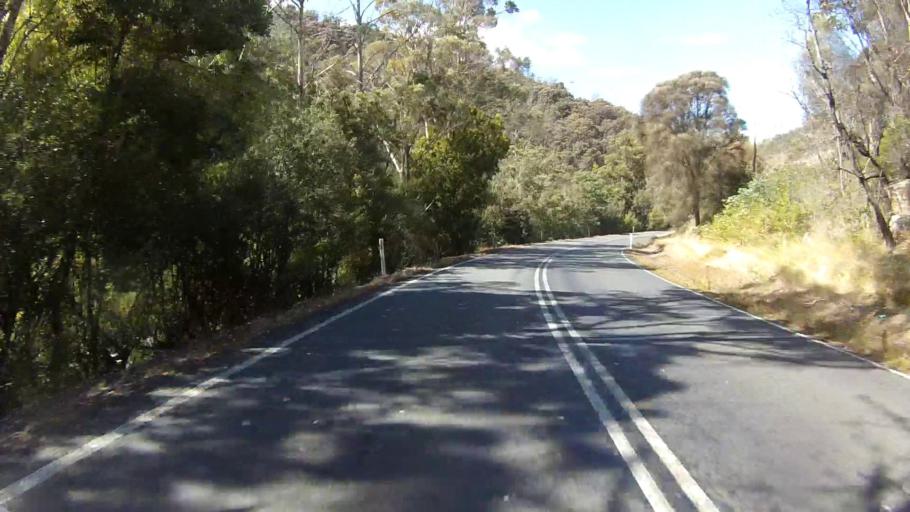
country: AU
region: Tasmania
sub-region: Derwent Valley
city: New Norfolk
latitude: -42.6788
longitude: 146.7659
